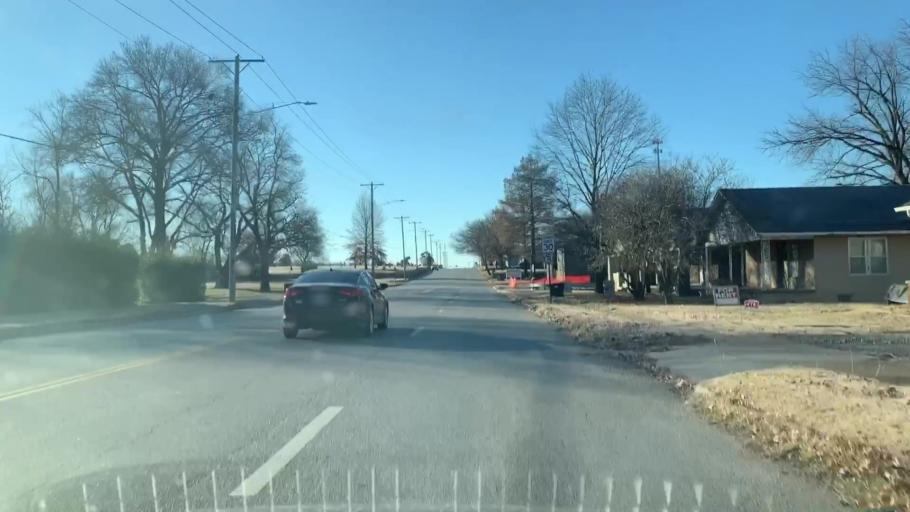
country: US
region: Kansas
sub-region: Crawford County
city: Pittsburg
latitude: 37.3868
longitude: -94.7052
